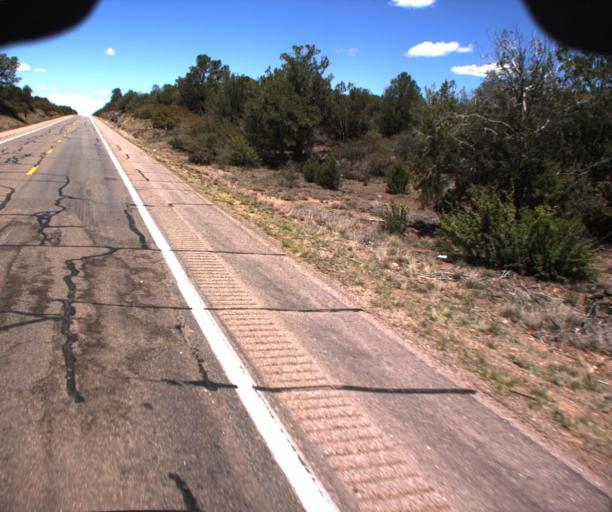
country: US
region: Arizona
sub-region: Yavapai County
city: Paulden
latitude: 35.0633
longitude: -112.3995
